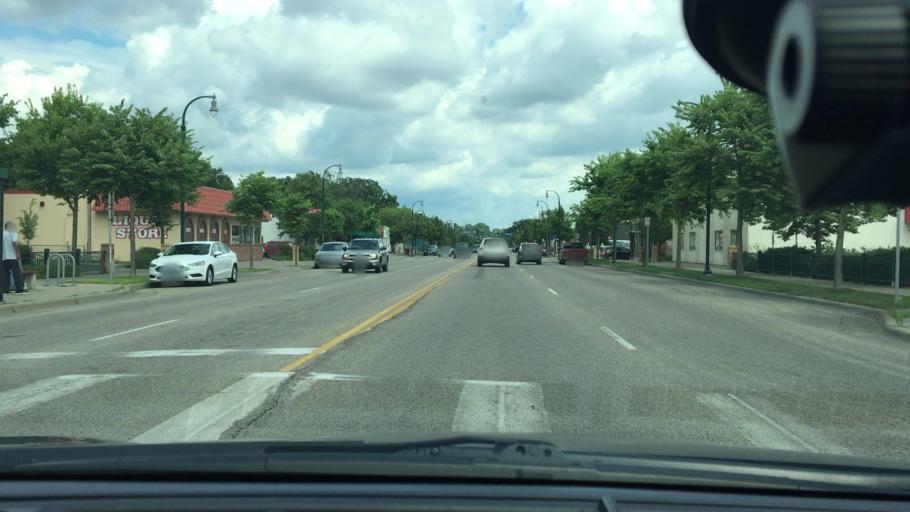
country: US
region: Minnesota
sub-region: Ramsey County
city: Lauderdale
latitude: 44.9484
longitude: -93.2165
